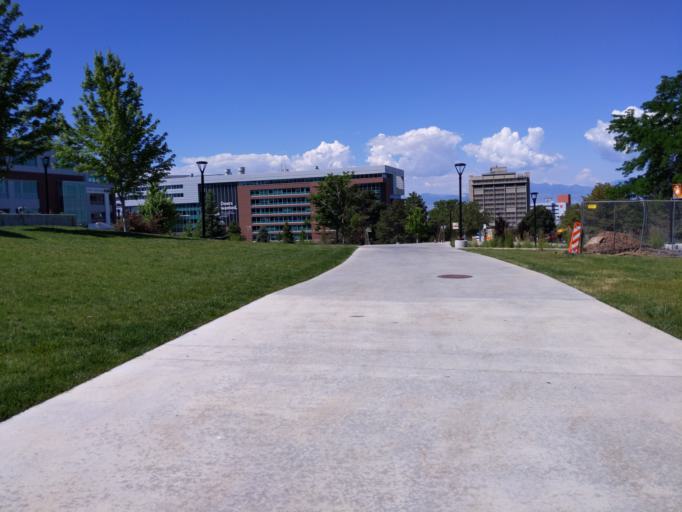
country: US
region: Utah
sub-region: Salt Lake County
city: Salt Lake City
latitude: 40.7634
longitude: -111.8421
